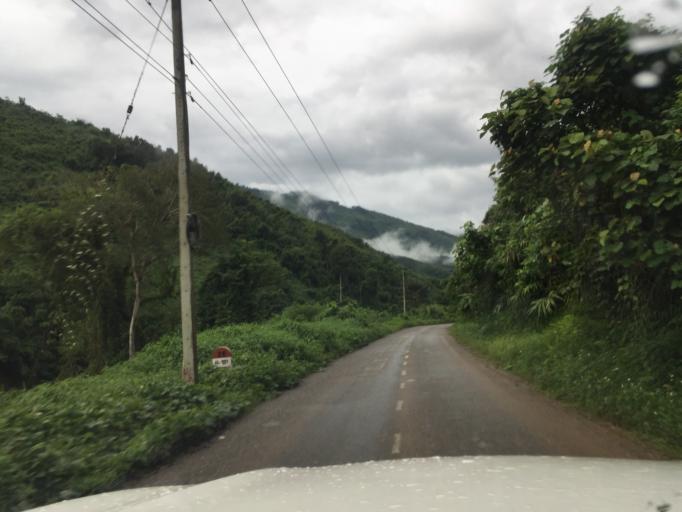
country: LA
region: Oudomxai
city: Muang La
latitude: 21.0201
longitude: 102.2324
